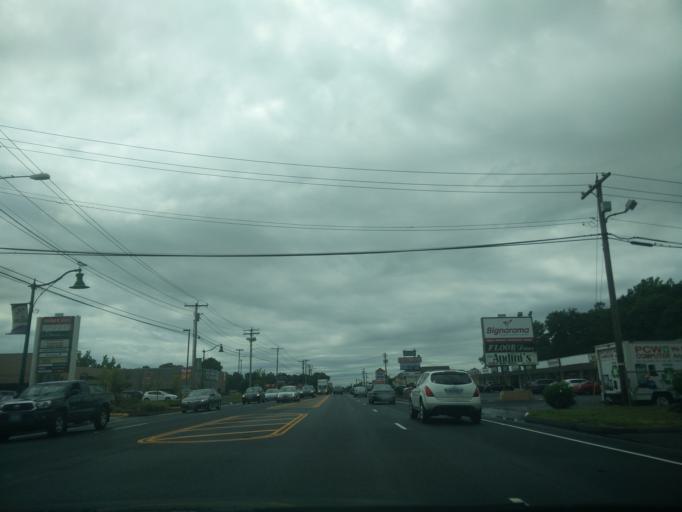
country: US
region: Connecticut
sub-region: New Haven County
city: Orange
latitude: 41.2525
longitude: -73.0192
